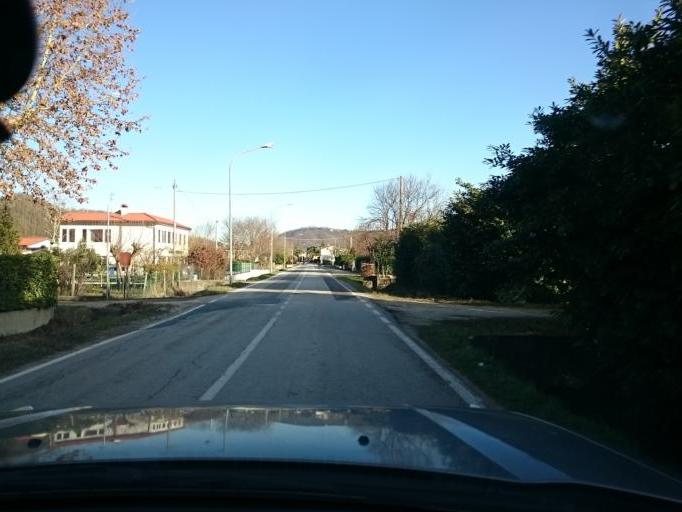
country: IT
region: Veneto
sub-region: Provincia di Padova
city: Treponti
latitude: 45.3659
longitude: 11.6972
